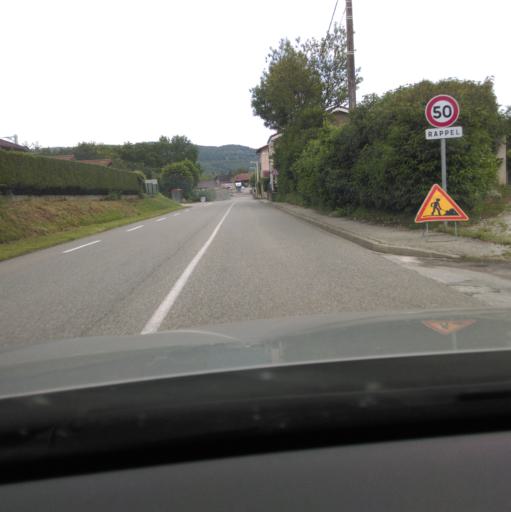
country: FR
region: Rhone-Alpes
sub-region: Departement de l'Ain
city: Izernore
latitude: 46.1864
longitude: 5.5454
